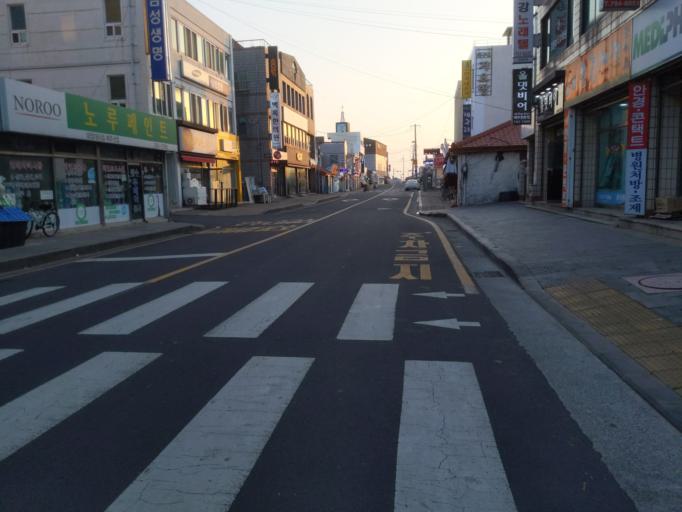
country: KR
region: Jeju-do
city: Gaigeturi
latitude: 33.2216
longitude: 126.2519
